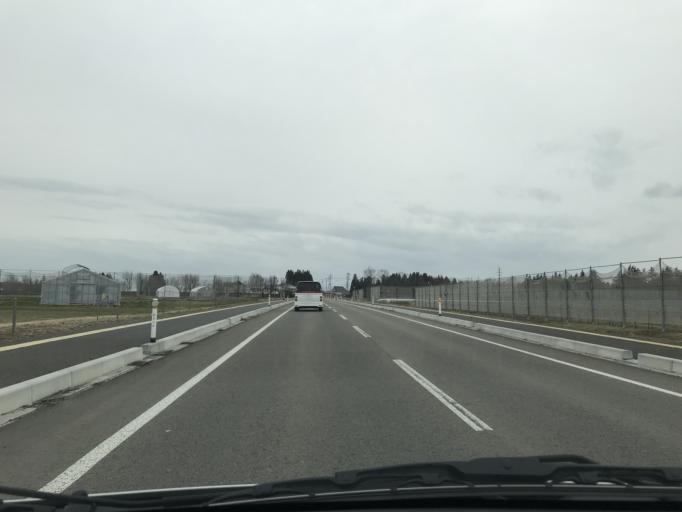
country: JP
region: Iwate
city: Hanamaki
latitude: 39.3544
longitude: 141.1059
